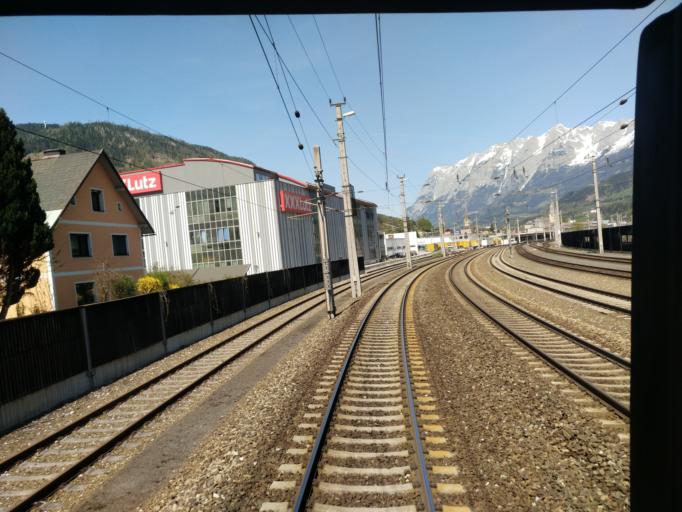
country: AT
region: Salzburg
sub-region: Politischer Bezirk Sankt Johann im Pongau
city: Bischofshofen
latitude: 47.4075
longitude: 13.2181
